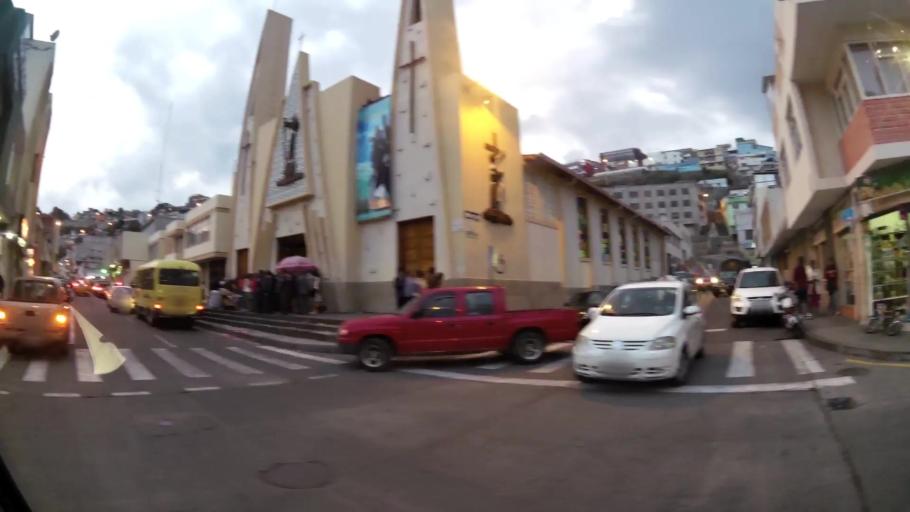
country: EC
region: Tungurahua
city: Ambato
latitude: -1.2447
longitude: -78.6314
